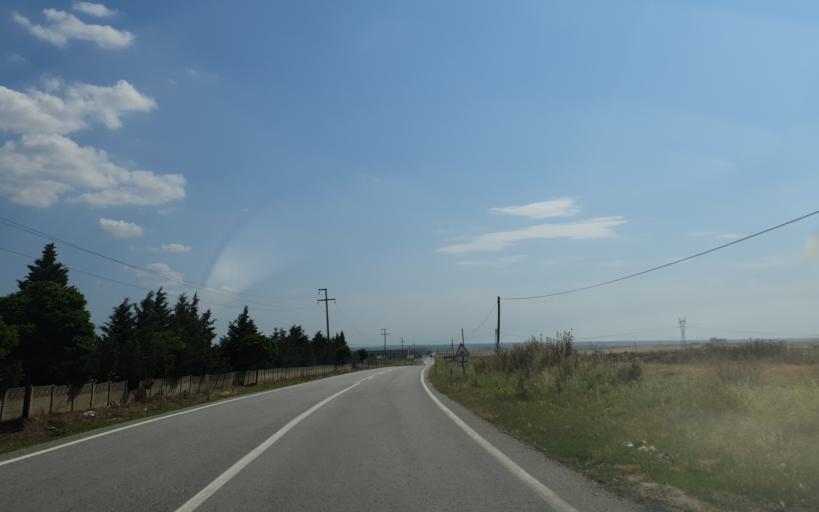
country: TR
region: Kirklareli
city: Buyukkaristiran
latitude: 41.3325
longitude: 27.5328
